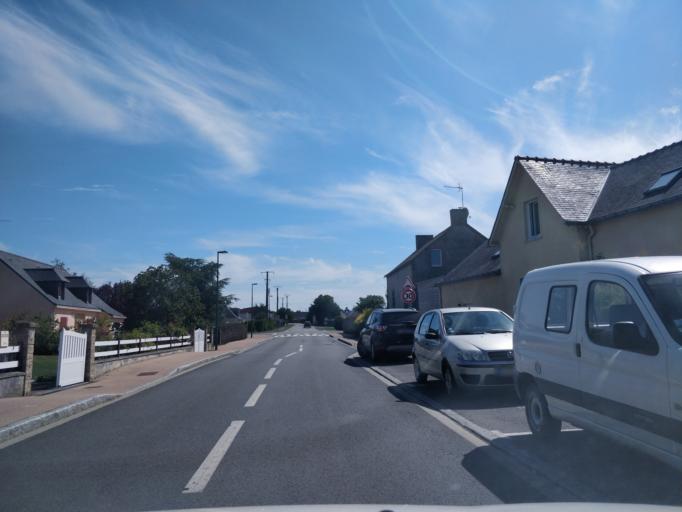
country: FR
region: Brittany
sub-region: Departement d'Ille-et-Vilaine
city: Grand-Fougeray
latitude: 47.6871
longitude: -1.7347
